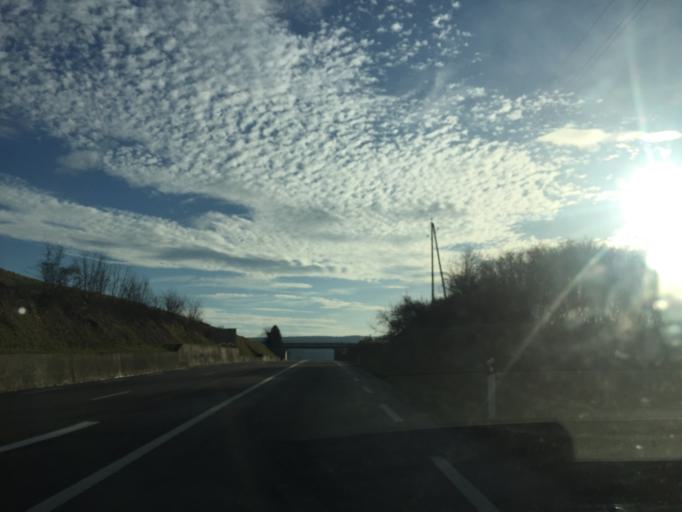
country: FR
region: Franche-Comte
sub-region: Departement du Jura
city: Arbois
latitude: 46.9314
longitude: 5.7759
